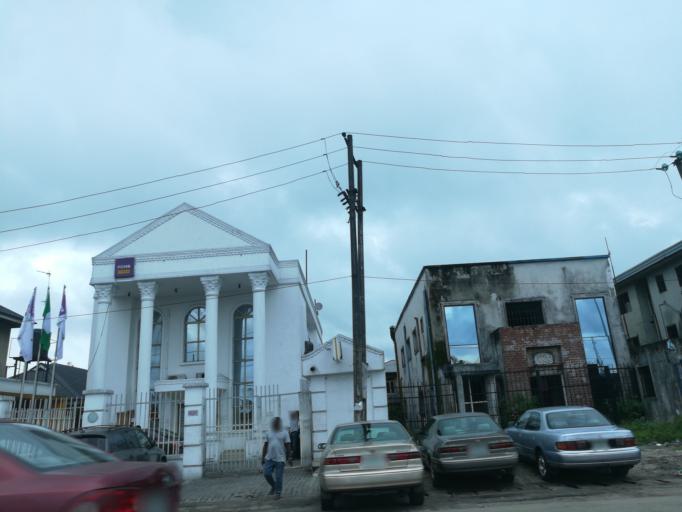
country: NG
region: Rivers
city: Port Harcourt
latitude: 4.7619
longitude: 7.0253
